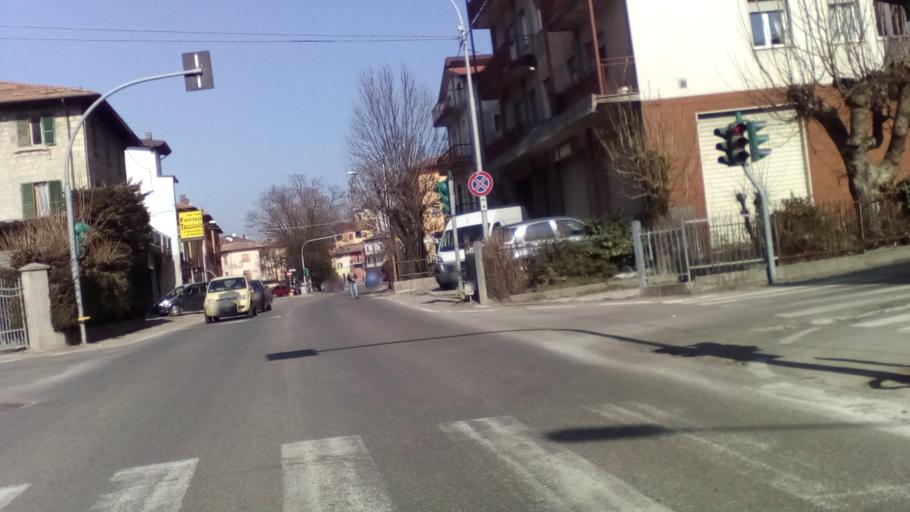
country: IT
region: Emilia-Romagna
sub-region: Provincia di Modena
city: Pavullo nel Frignano
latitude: 44.3379
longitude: 10.8327
